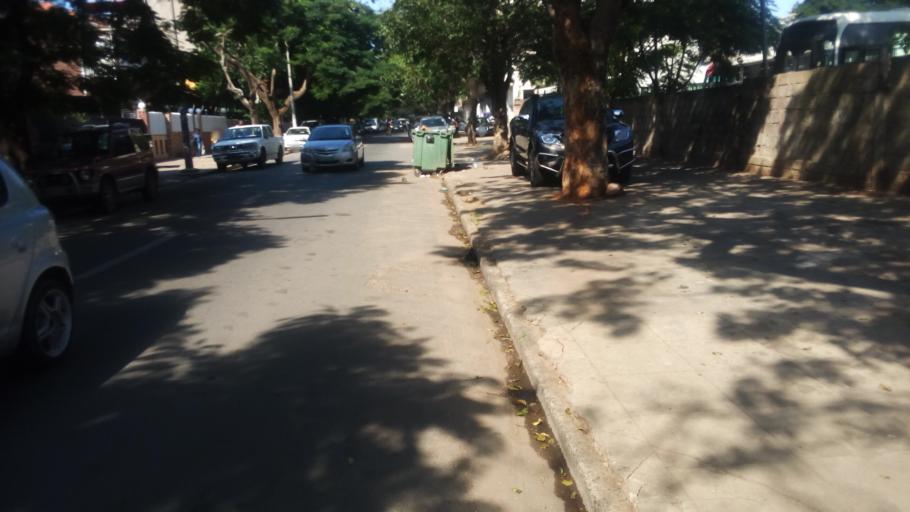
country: MZ
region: Maputo City
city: Maputo
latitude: -25.9606
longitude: 32.5758
